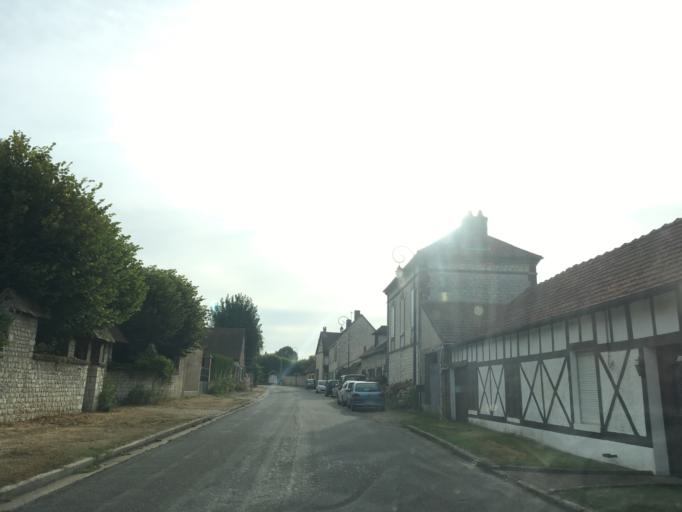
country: FR
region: Ile-de-France
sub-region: Departement des Yvelines
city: Limetz-Villez
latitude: 49.1050
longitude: 1.5310
